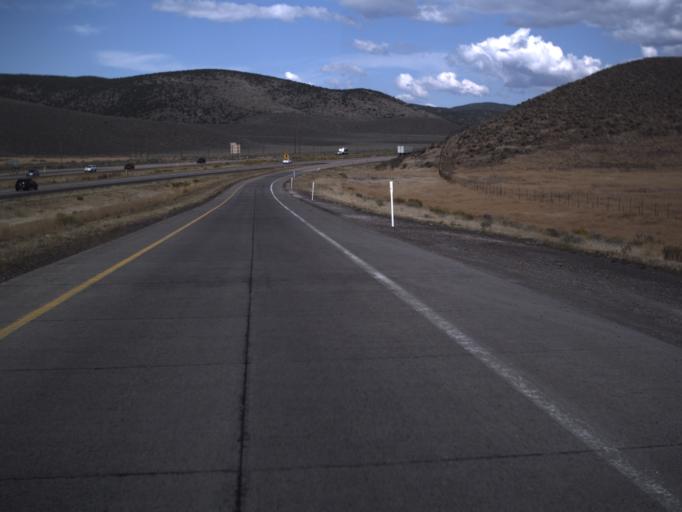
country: US
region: Utah
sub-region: Beaver County
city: Beaver
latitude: 38.0723
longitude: -112.6872
